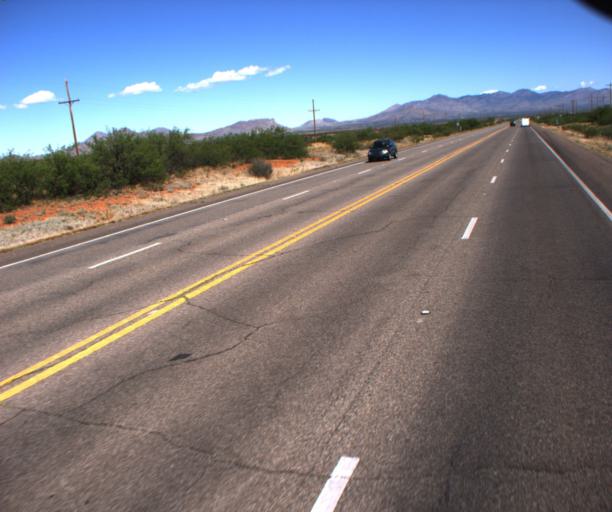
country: US
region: Arizona
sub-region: Cochise County
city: Huachuca City
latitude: 31.6020
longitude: -110.3281
